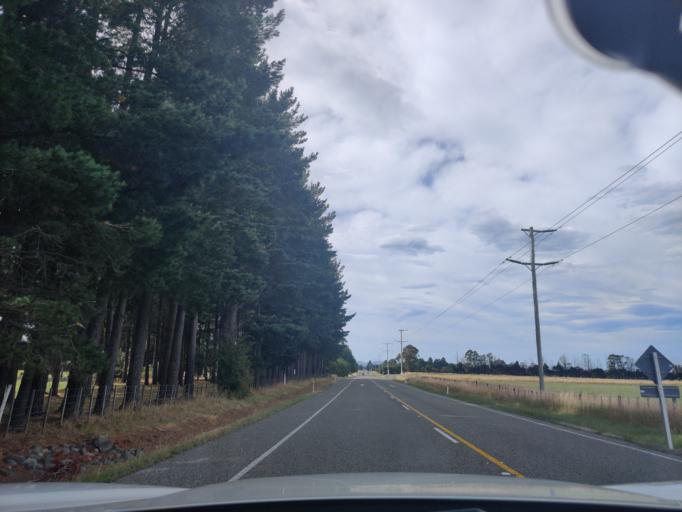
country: NZ
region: Wellington
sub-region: Masterton District
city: Masterton
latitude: -40.8440
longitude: 175.6322
